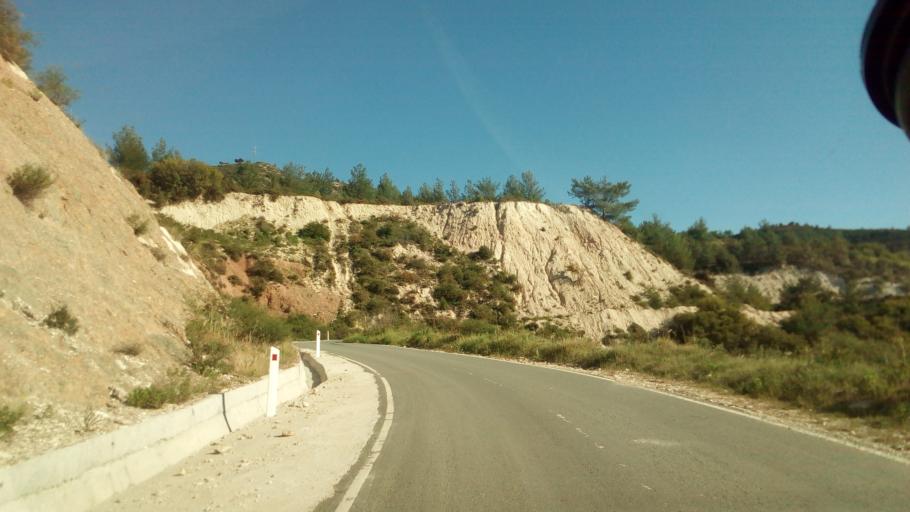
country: CY
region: Limassol
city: Pachna
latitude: 34.8793
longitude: 32.7507
